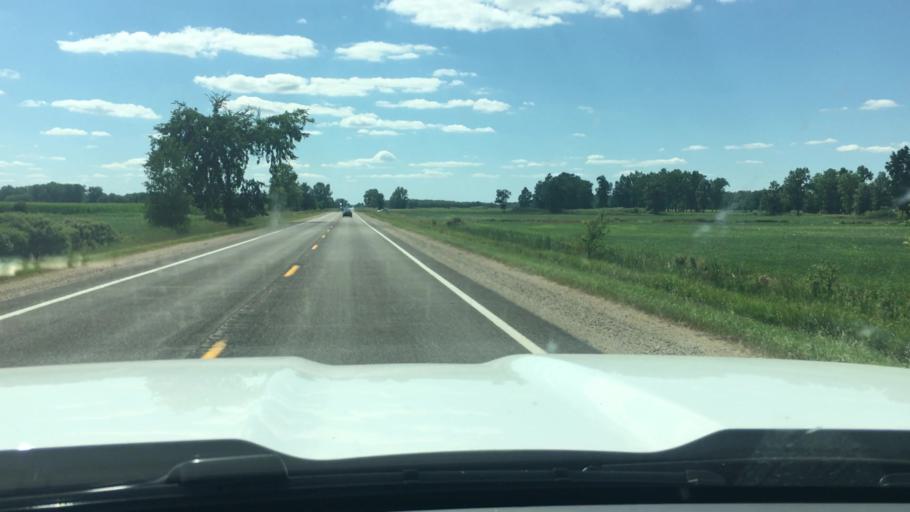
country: US
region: Michigan
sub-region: Clinton County
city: Ovid
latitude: 43.1759
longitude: -84.4160
